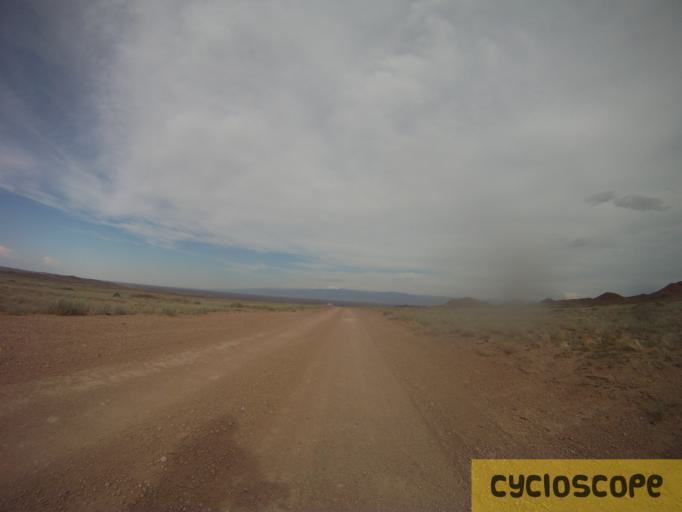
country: KZ
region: Almaty Oblysy
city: Kegen
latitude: 43.3622
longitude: 79.0440
